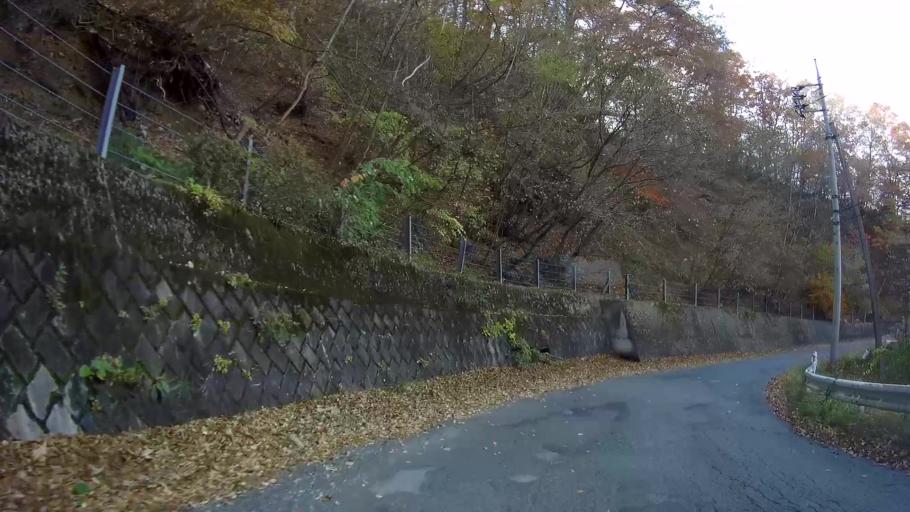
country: JP
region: Gunma
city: Nakanojomachi
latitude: 36.6236
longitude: 138.6316
